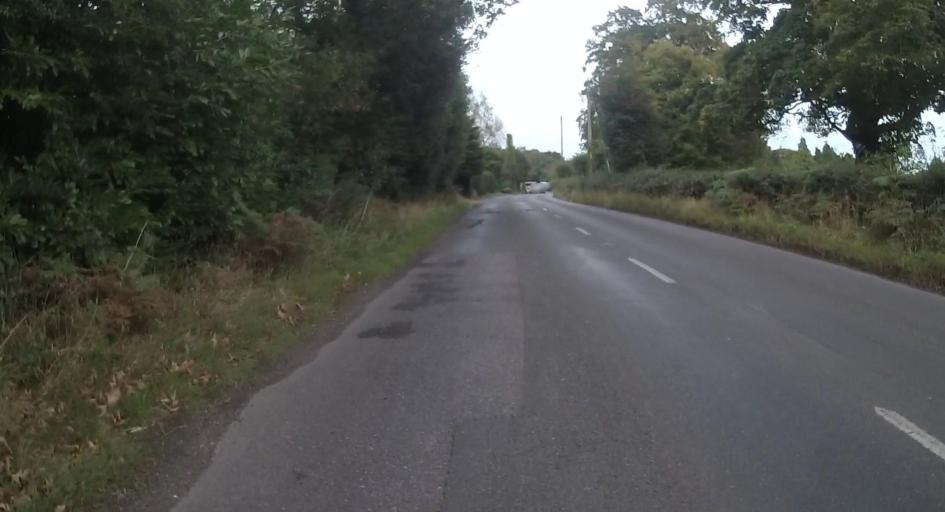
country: GB
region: England
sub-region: West Berkshire
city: Thatcham
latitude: 51.4141
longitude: -1.2322
